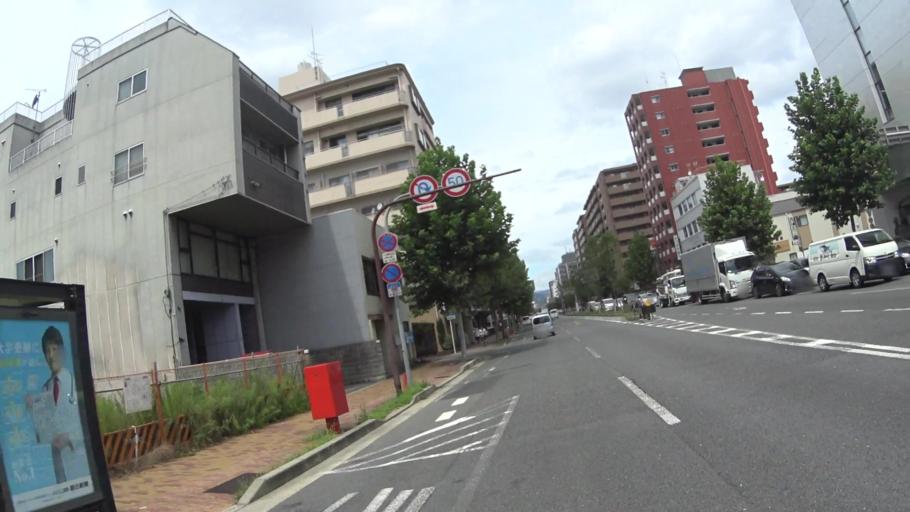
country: JP
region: Kyoto
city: Kyoto
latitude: 34.9967
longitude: 135.7321
